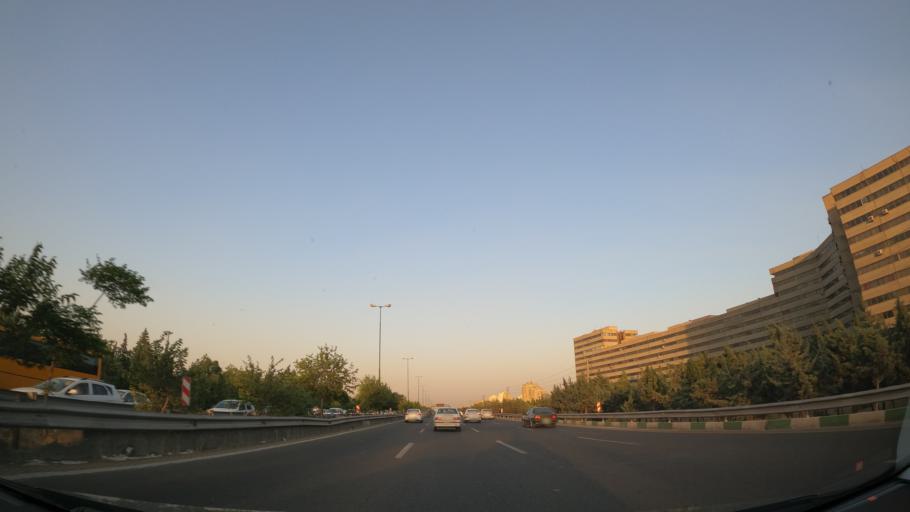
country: IR
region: Tehran
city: Tehran
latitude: 35.7160
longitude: 51.3175
